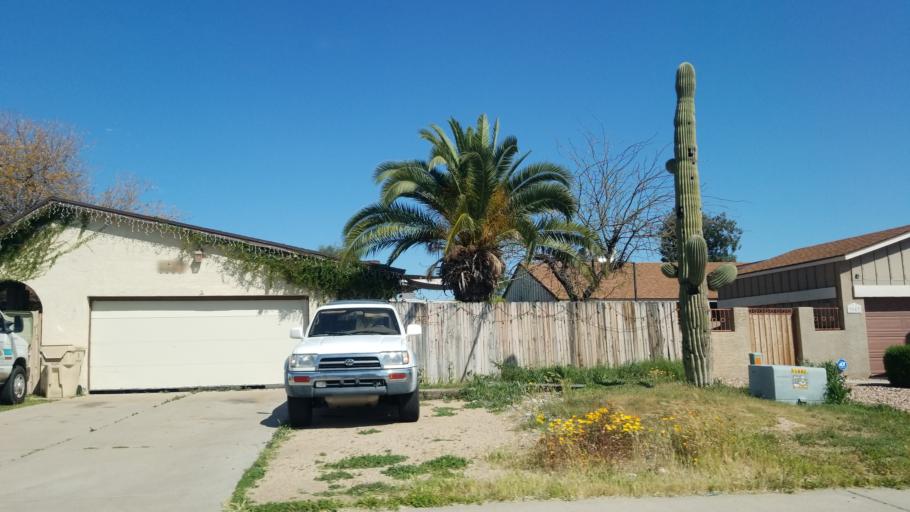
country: US
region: Arizona
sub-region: Maricopa County
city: Glendale
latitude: 33.5726
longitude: -112.1776
